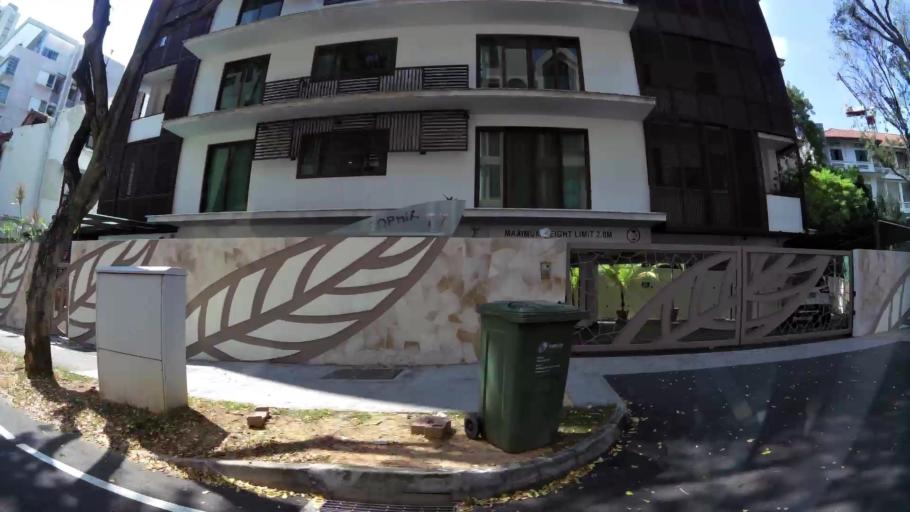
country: SG
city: Singapore
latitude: 1.3019
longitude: 103.8478
